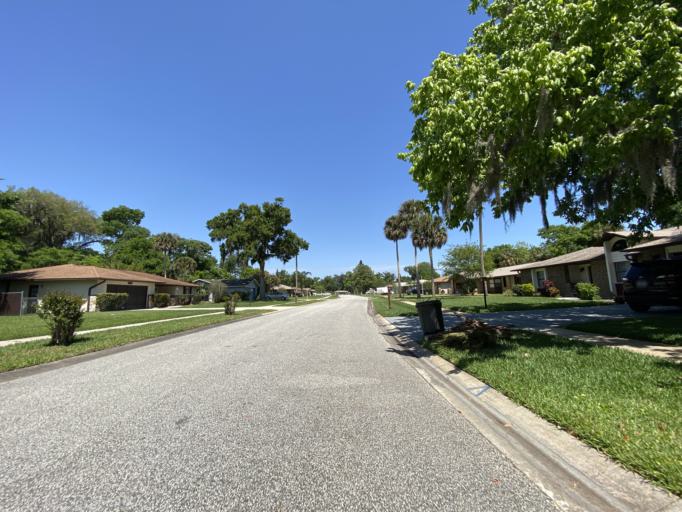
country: US
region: Florida
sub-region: Volusia County
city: South Daytona
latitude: 29.1500
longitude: -81.0097
